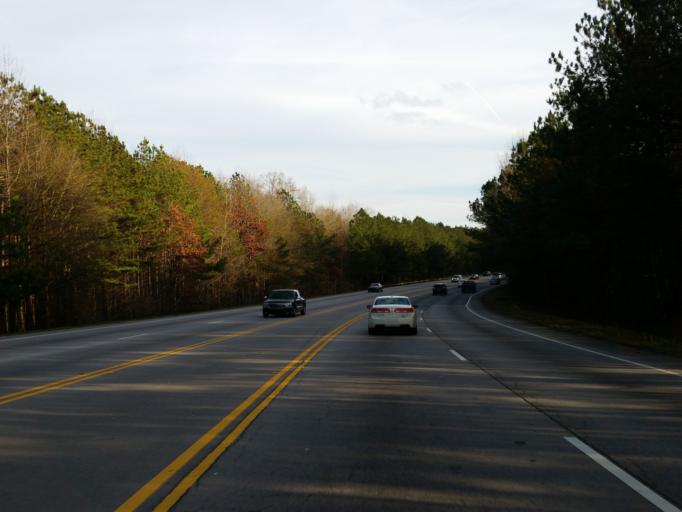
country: US
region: Georgia
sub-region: Cobb County
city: Powder Springs
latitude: 33.8732
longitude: -84.6989
